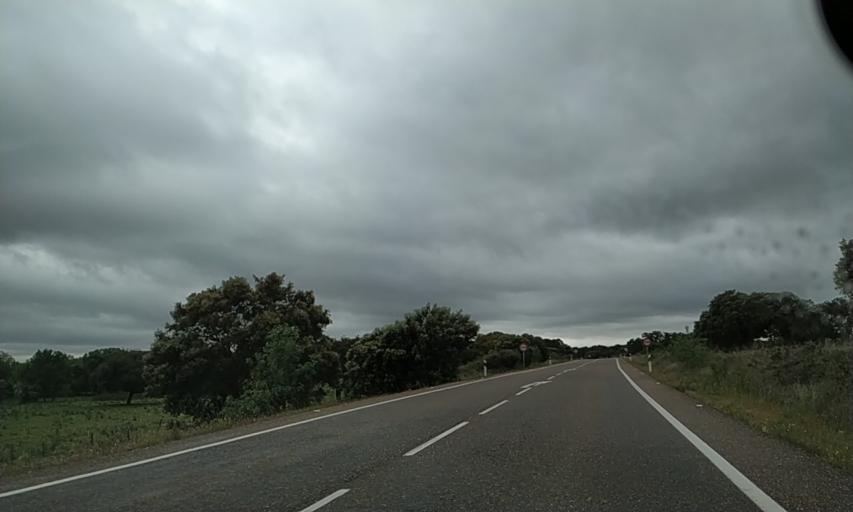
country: ES
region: Extremadura
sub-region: Provincia de Badajoz
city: La Roca de la Sierra
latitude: 39.0706
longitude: -6.7560
